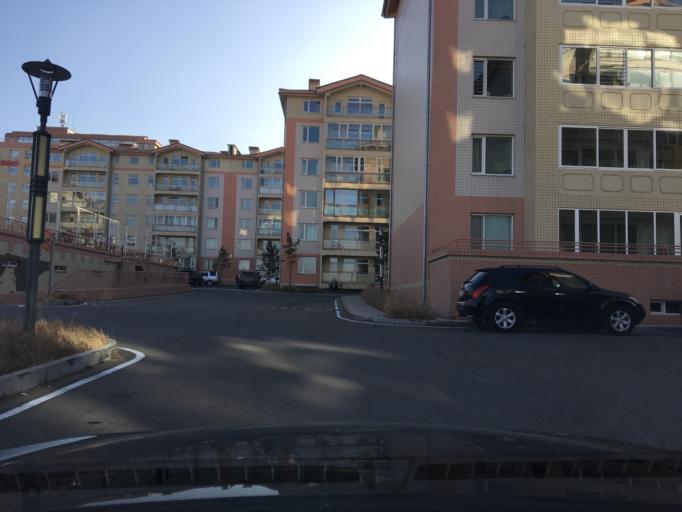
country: MN
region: Ulaanbaatar
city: Ulaanbaatar
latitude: 47.8771
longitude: 106.9098
